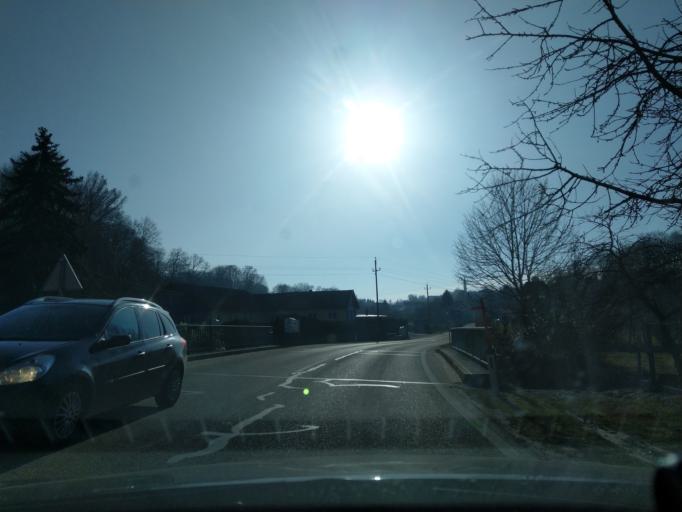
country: DE
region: Bavaria
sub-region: Lower Bavaria
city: Bad Fussing
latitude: 48.3281
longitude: 13.3464
